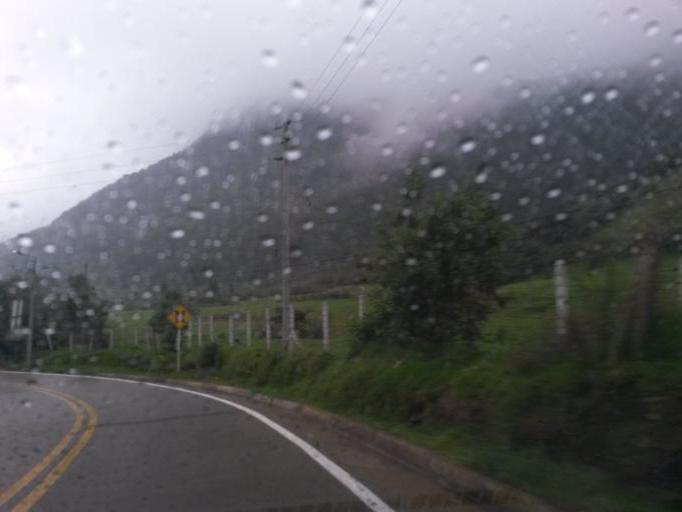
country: CO
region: Cauca
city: Paispamba
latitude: 2.3374
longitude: -76.4967
